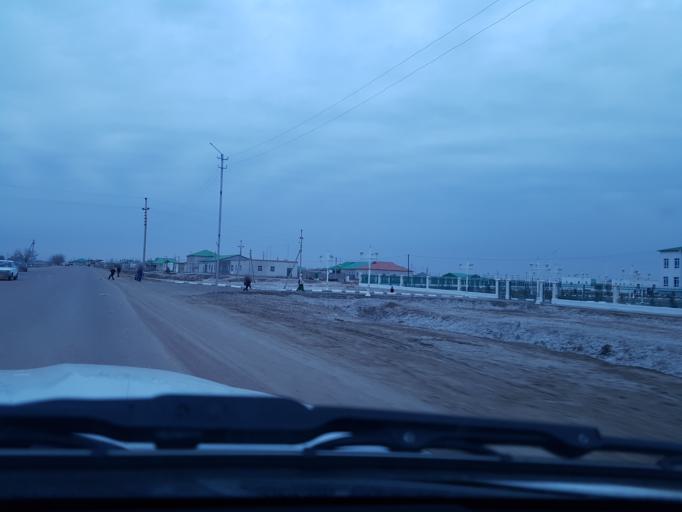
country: TM
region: Dasoguz
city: Yylanly
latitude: 41.8925
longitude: 59.6158
